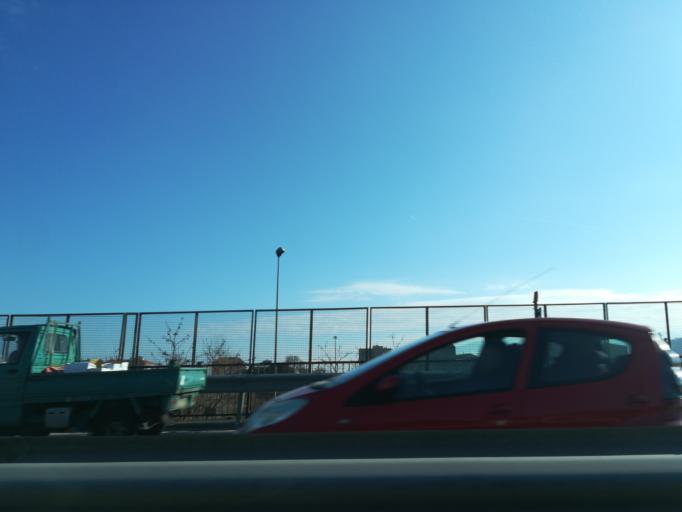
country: IT
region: Liguria
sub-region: Provincia di Savona
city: Vado Ligure
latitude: 44.2754
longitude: 8.4350
